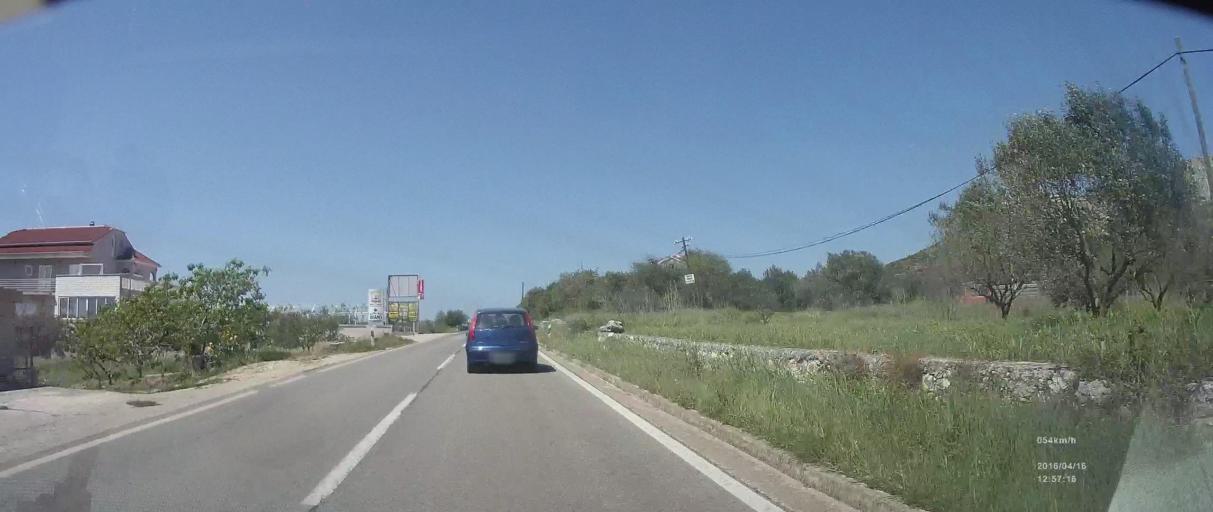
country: HR
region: Sibensko-Kniniska
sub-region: Grad Sibenik
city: Brodarica
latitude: 43.7045
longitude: 15.9334
